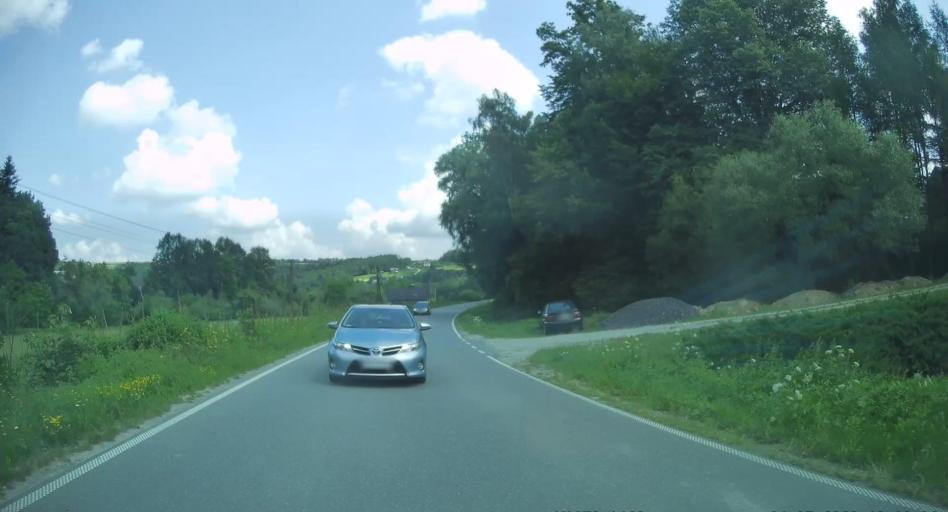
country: PL
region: Lesser Poland Voivodeship
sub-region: Powiat nowosadecki
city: Korzenna
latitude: 49.7497
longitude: 20.7706
